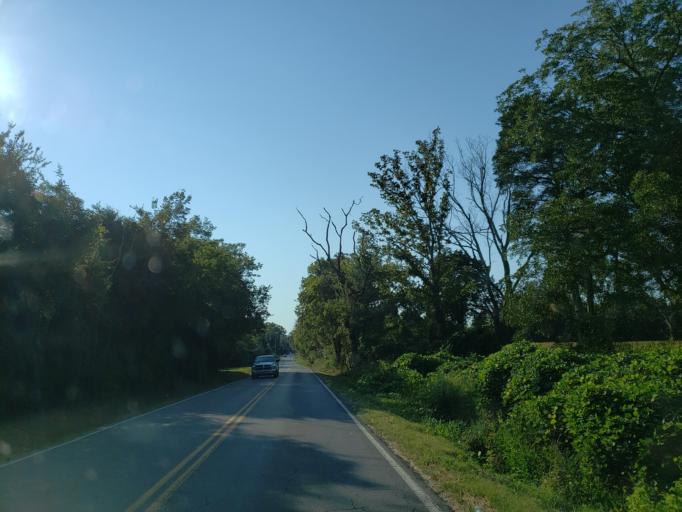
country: US
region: Tennessee
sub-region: Bradley County
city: Wildwood Lake
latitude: 35.1037
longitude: -84.8143
